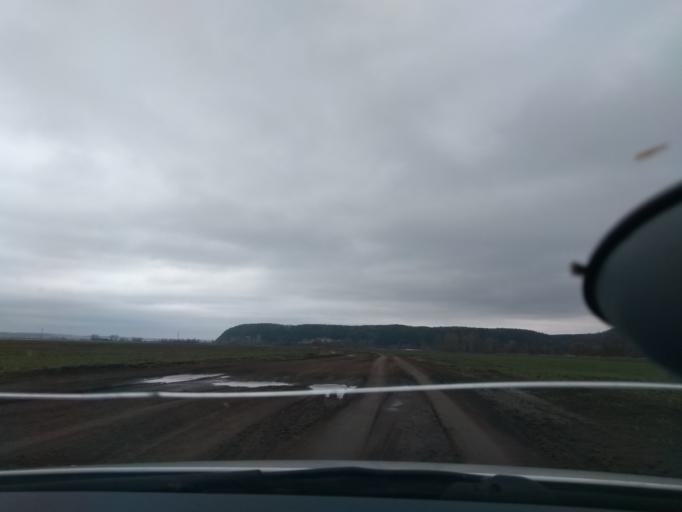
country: RU
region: Perm
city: Orda
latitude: 57.2516
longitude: 56.6223
